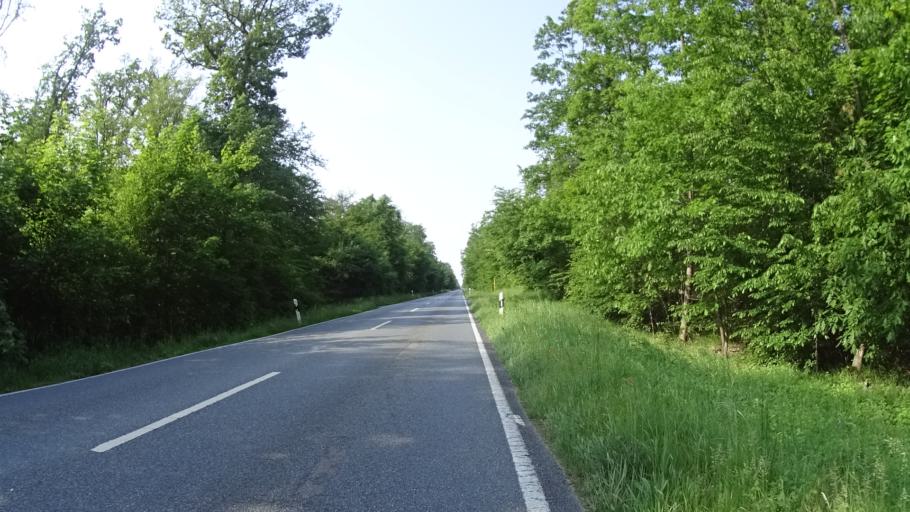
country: DE
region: Baden-Wuerttemberg
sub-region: Karlsruhe Region
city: Reilingen
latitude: 49.2806
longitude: 8.5640
